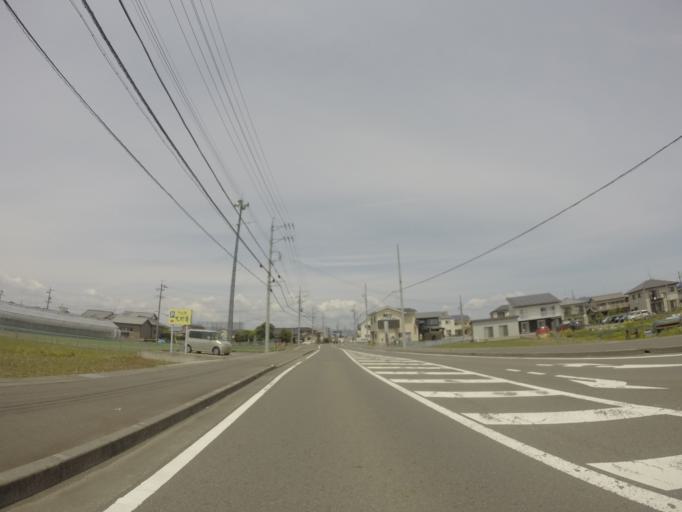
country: JP
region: Shizuoka
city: Fujieda
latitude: 34.8431
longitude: 138.2928
